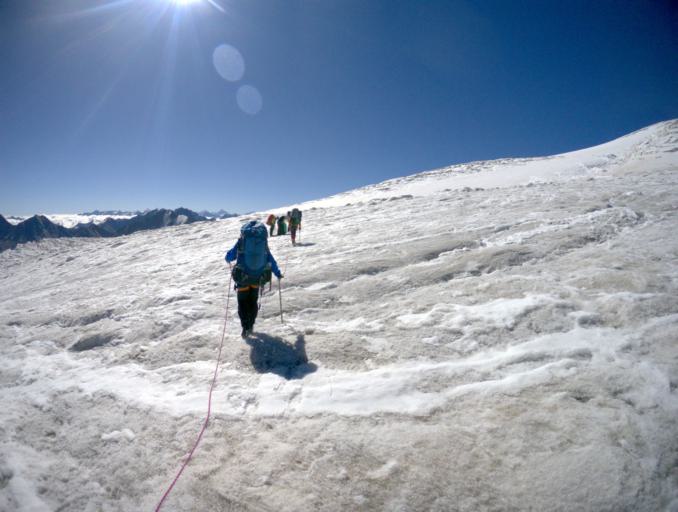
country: RU
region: Kabardino-Balkariya
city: Terskol
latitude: 43.3658
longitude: 42.4953
